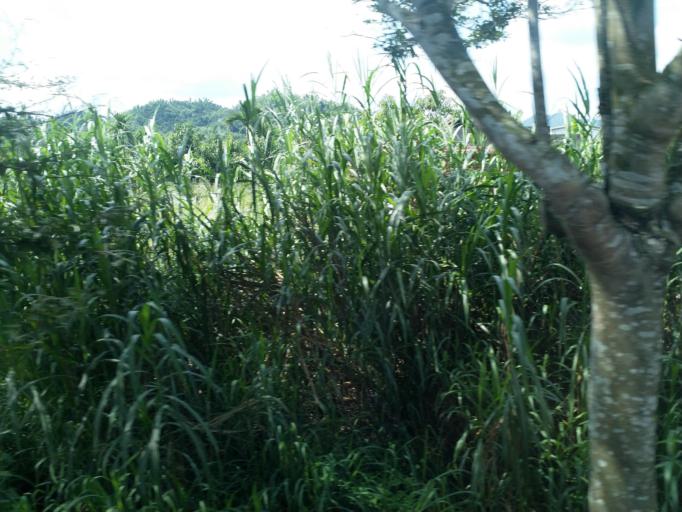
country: TW
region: Taiwan
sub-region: Pingtung
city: Pingtung
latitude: 22.8887
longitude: 120.5794
